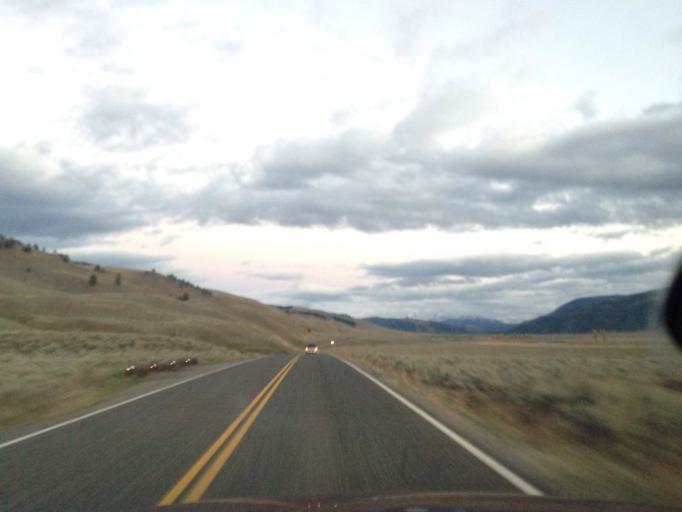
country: US
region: Montana
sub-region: Park County
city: Livingston
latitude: 44.8928
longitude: -110.2323
